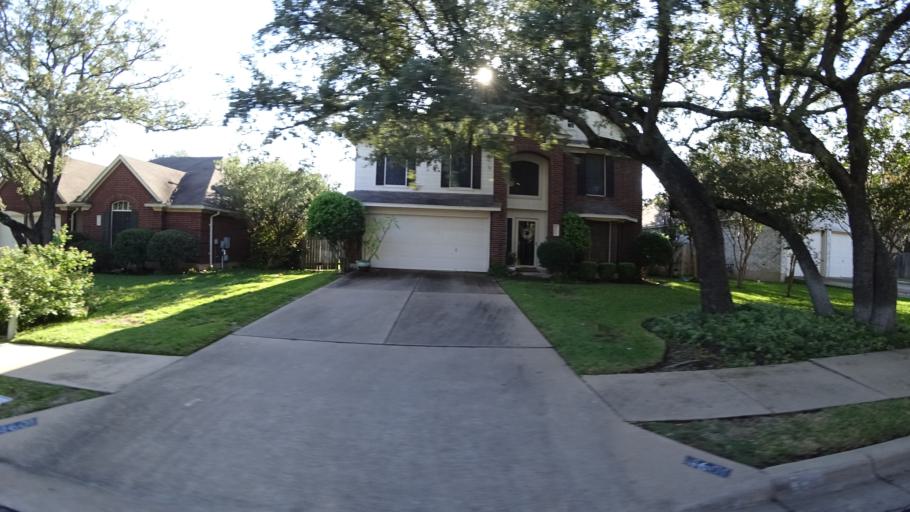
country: US
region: Texas
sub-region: Travis County
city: Shady Hollow
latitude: 30.2042
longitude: -97.8554
